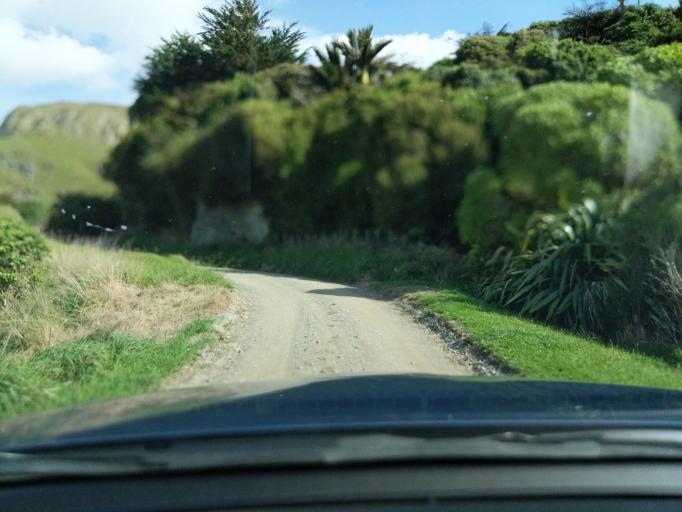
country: NZ
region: Tasman
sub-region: Tasman District
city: Takaka
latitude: -40.6439
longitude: 172.4318
